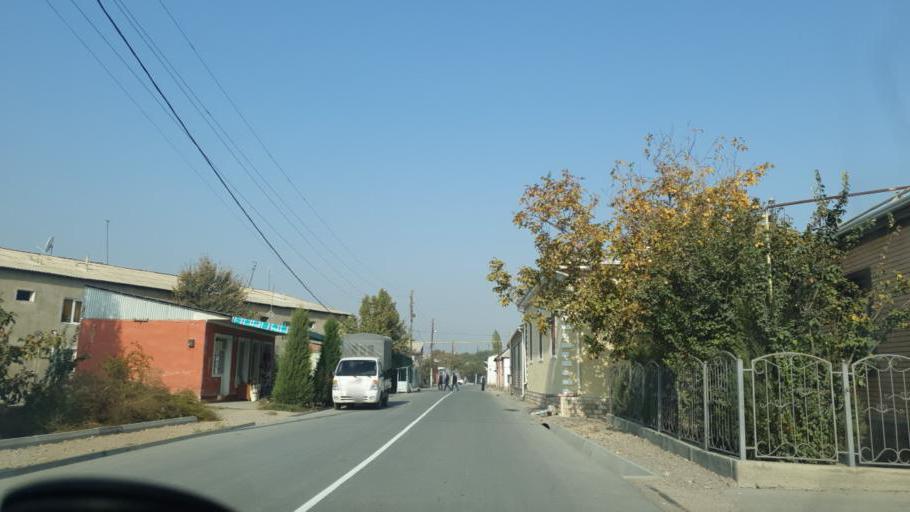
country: UZ
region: Fergana
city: Qo`qon
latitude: 40.5827
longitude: 70.9101
